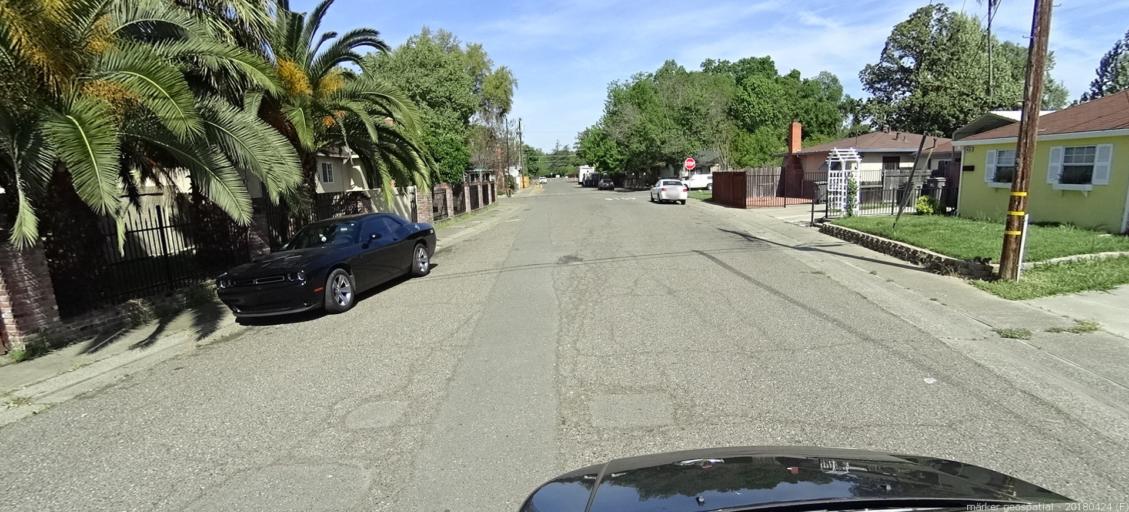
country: US
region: California
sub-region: Yolo County
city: West Sacramento
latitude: 38.5655
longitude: -121.5284
